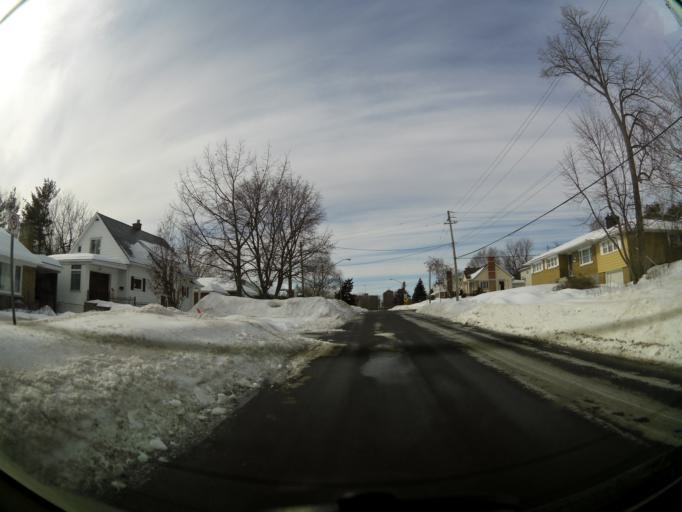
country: CA
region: Ontario
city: Ottawa
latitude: 45.4450
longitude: -75.6098
